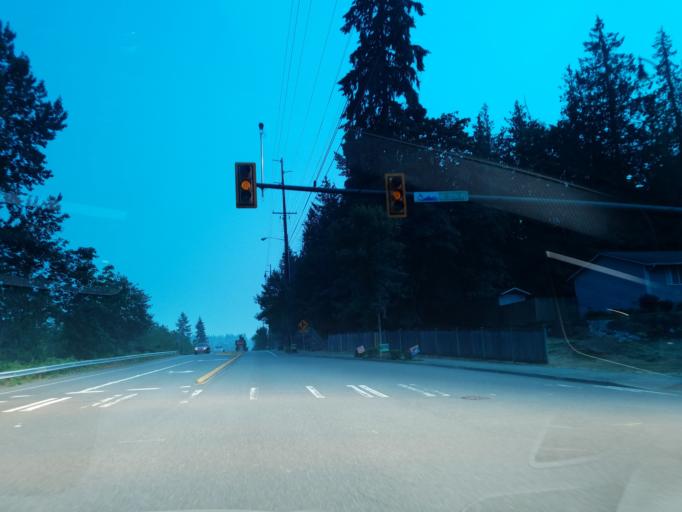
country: US
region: Washington
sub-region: King County
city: City of Sammamish
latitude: 47.6206
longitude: -122.0356
